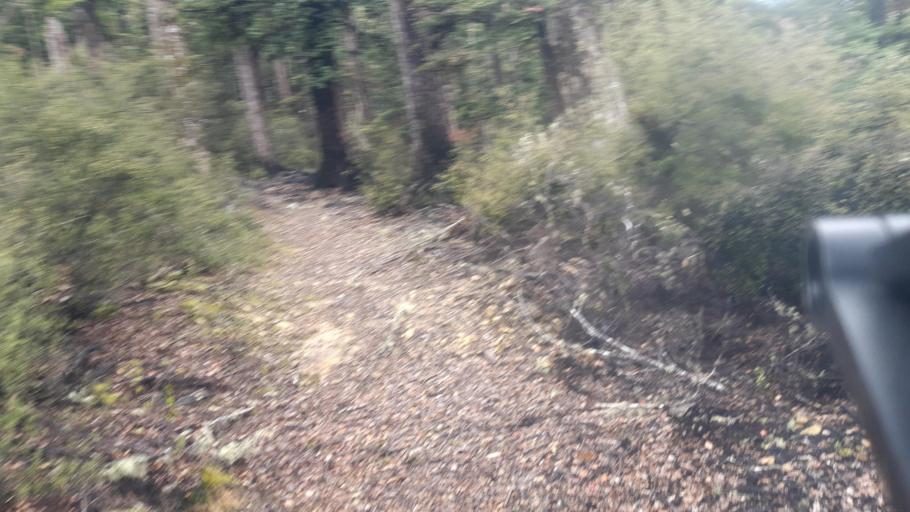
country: NZ
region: Tasman
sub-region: Tasman District
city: Wakefield
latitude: -41.7590
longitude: 172.8060
